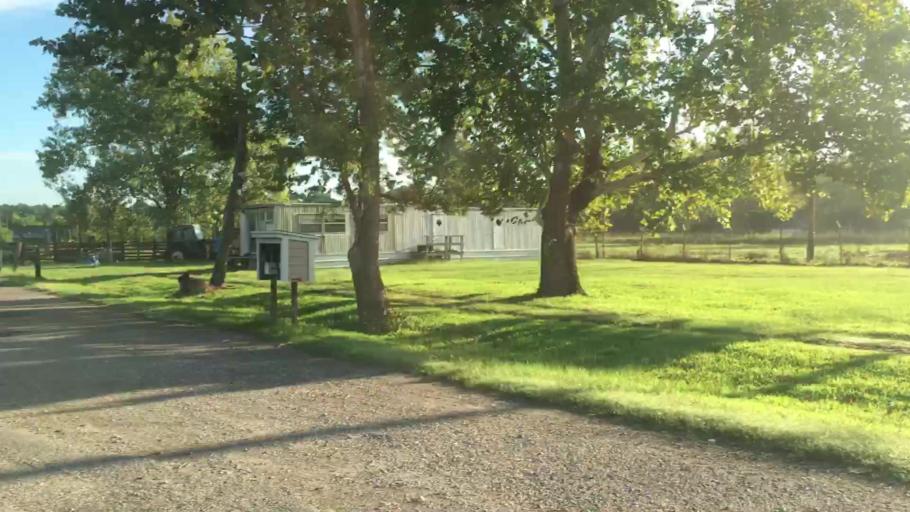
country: US
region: Texas
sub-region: Harris County
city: Humble
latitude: 29.9593
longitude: -95.2597
